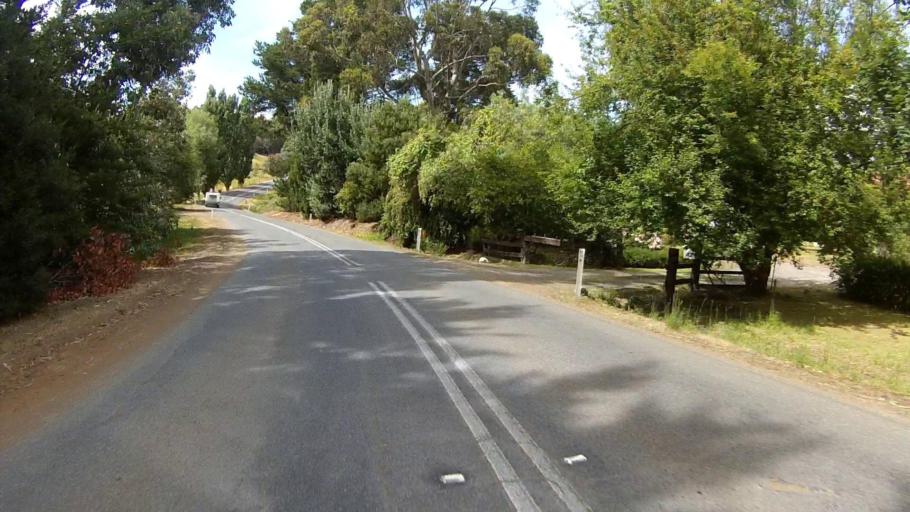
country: AU
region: Tasmania
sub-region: Kingborough
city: Kettering
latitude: -43.2078
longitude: 147.2550
